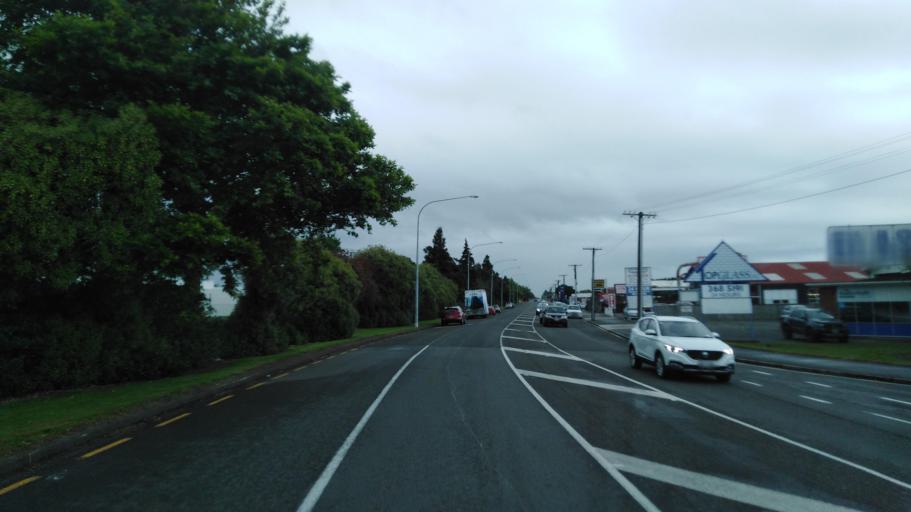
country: NZ
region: Manawatu-Wanganui
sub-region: Horowhenua District
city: Levin
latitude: -40.6332
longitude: 175.2757
